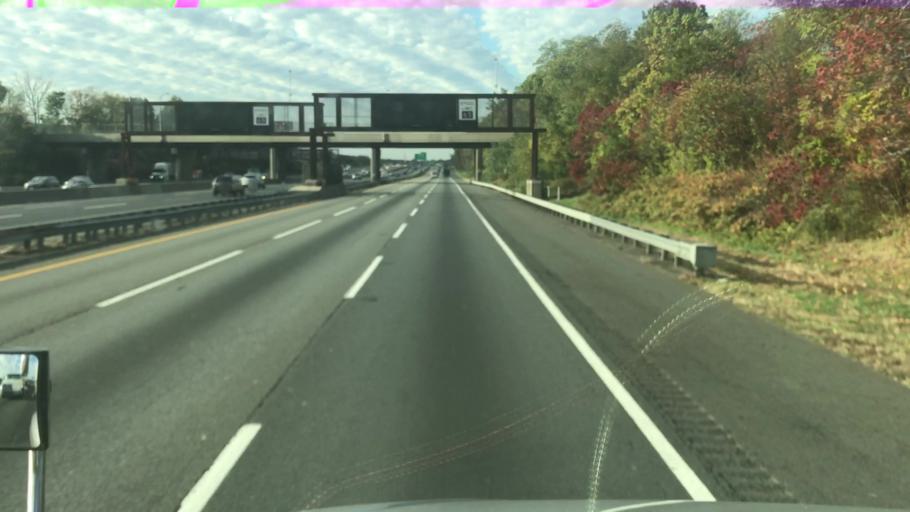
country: US
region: New Jersey
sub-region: Middlesex County
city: Piscataway
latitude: 40.4975
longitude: -74.3866
